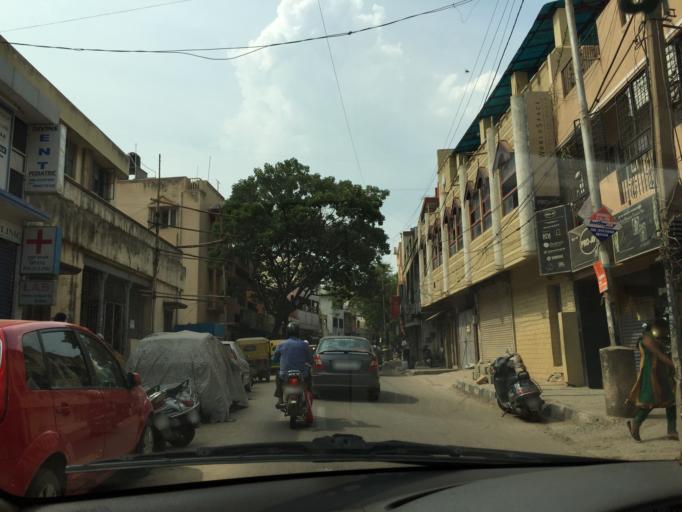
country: IN
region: Karnataka
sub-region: Bangalore Urban
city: Bangalore
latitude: 12.9850
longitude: 77.6118
